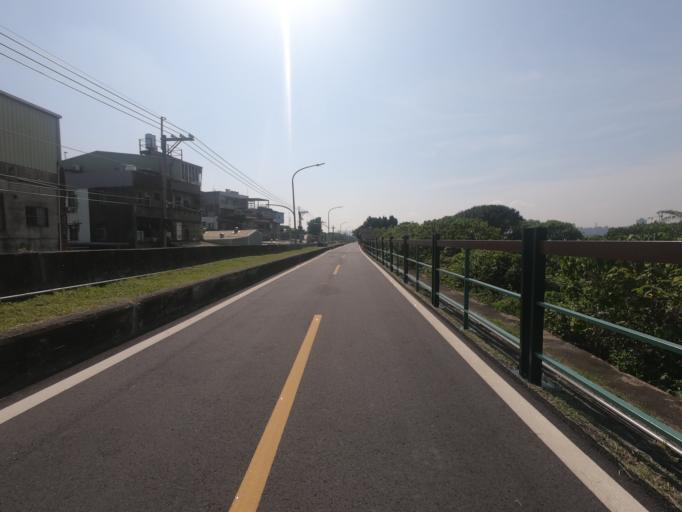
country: TW
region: Taipei
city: Taipei
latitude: 25.1057
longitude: 121.4743
